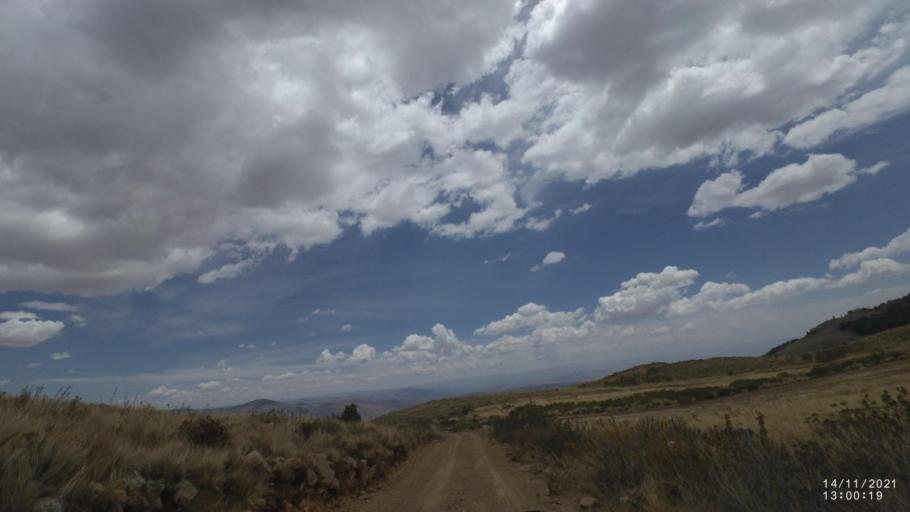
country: BO
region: Cochabamba
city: Colomi
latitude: -17.3634
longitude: -65.9775
